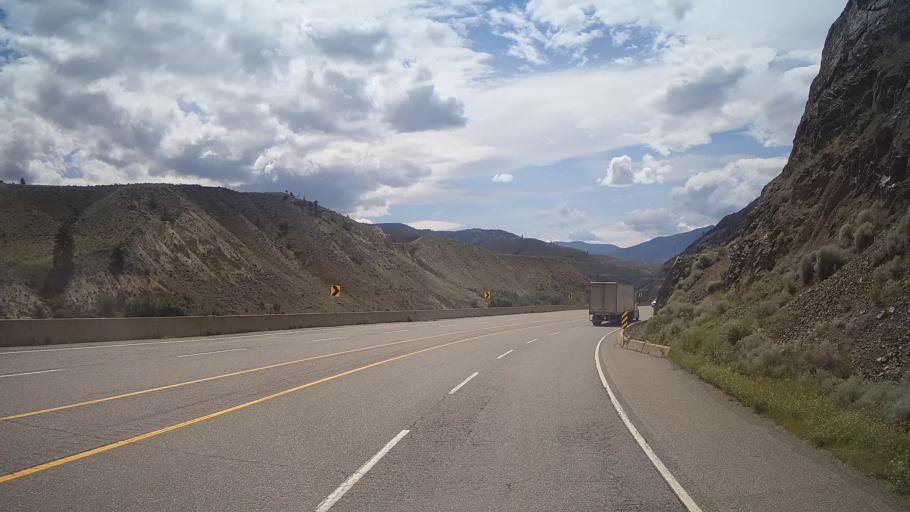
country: CA
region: British Columbia
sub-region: Thompson-Nicola Regional District
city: Ashcroft
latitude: 50.5128
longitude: -121.2830
